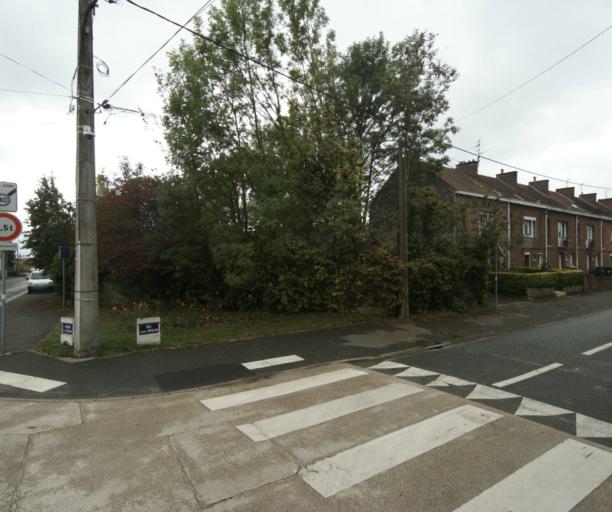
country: FR
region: Nord-Pas-de-Calais
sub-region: Departement du Nord
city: Wavrin
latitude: 50.5753
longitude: 2.9336
